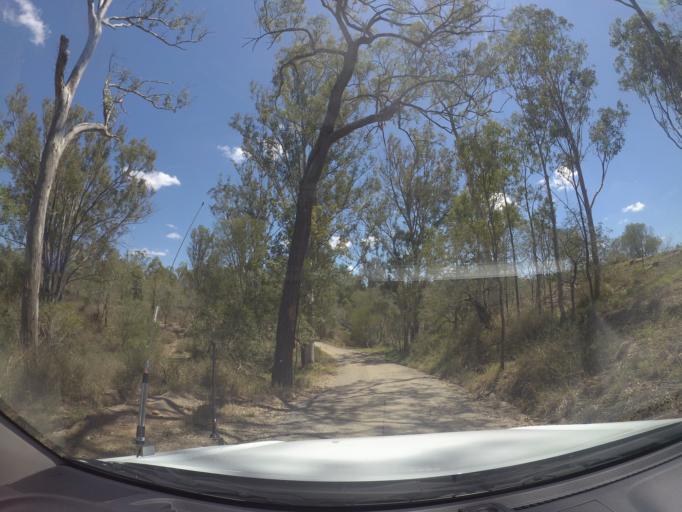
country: AU
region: Queensland
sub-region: Logan
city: North Maclean
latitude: -27.8386
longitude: 152.8741
